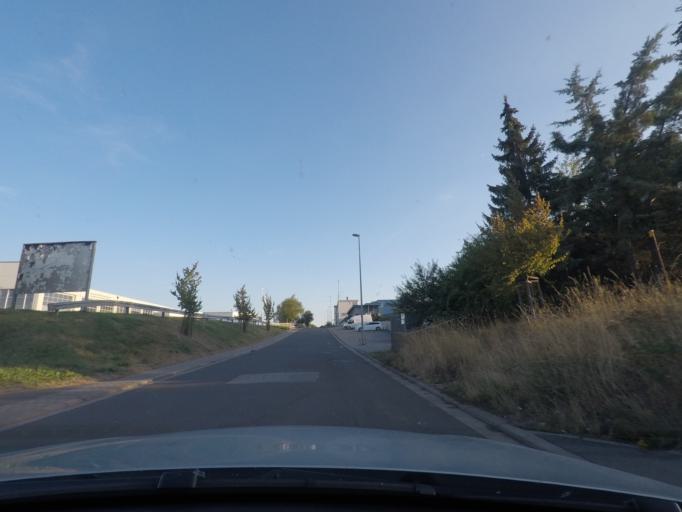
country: DE
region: Rheinland-Pfalz
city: Kirchheimbolanden
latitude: 49.6741
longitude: 8.0134
